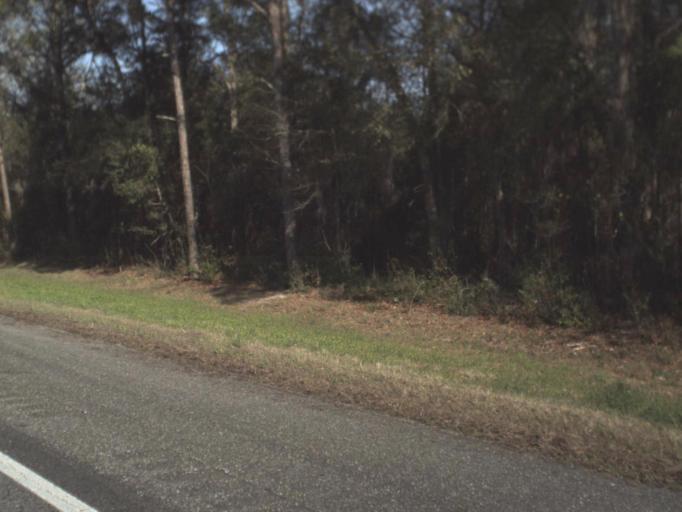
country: US
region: Florida
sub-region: Jefferson County
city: Monticello
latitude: 30.4704
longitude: -83.8145
